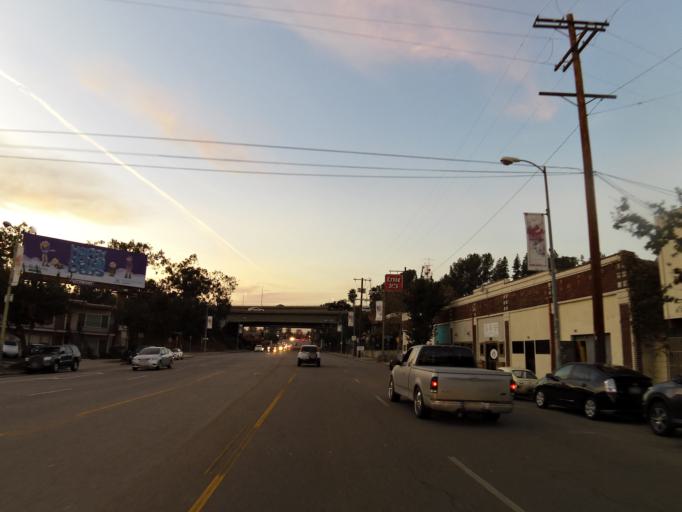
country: US
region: California
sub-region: Los Angeles County
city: Glendale
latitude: 34.1433
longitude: -118.2252
